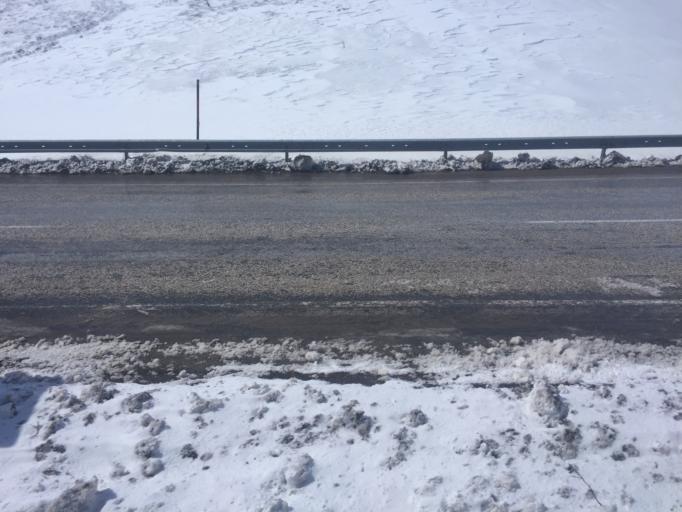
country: TR
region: Kahramanmaras
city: Goksun
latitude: 38.1974
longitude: 36.4559
